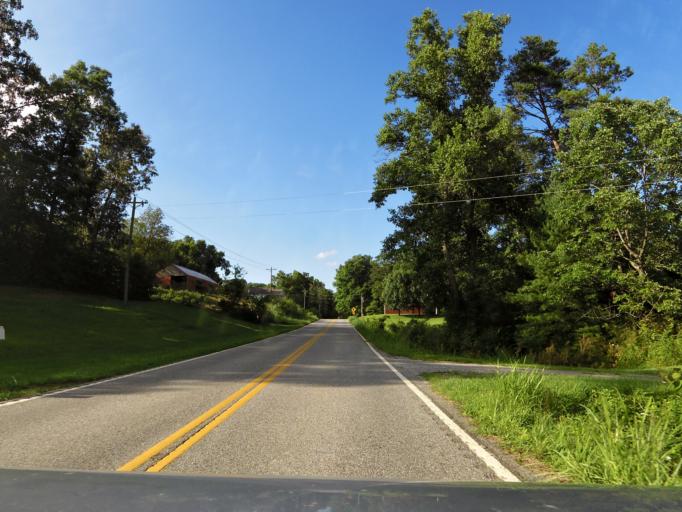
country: US
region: Tennessee
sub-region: Blount County
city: Maryville
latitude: 35.6253
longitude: -84.0249
